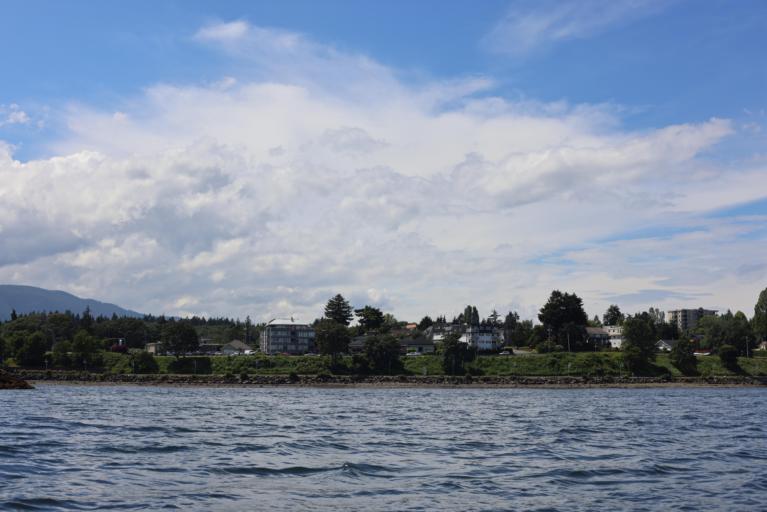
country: CA
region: British Columbia
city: Nanaimo
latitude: 49.1734
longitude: -123.9364
